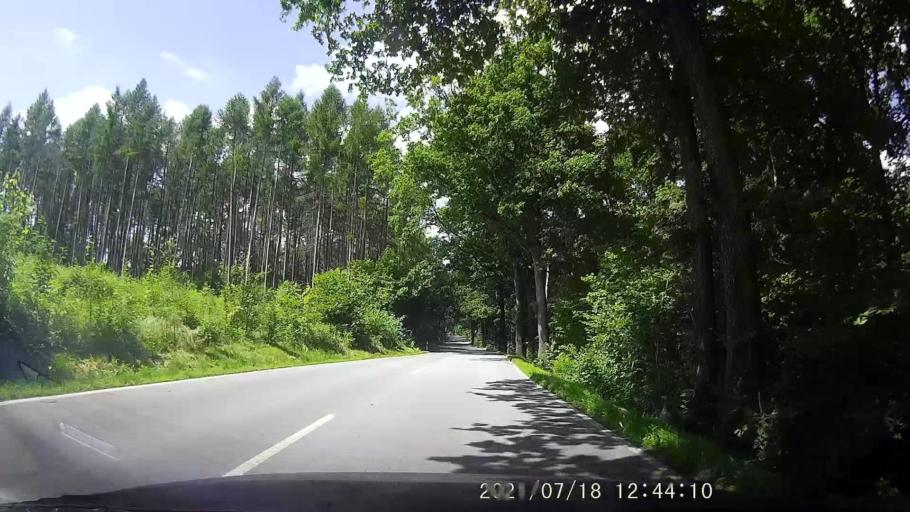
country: DE
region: Saxony
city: Reichenbach
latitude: 51.1842
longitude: 14.8170
